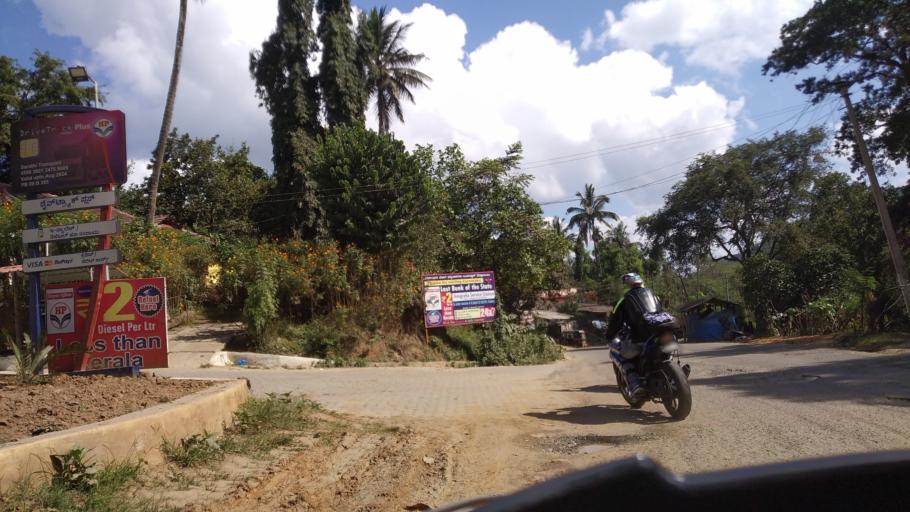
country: IN
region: Karnataka
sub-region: Kodagu
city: Ponnampet
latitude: 11.9673
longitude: 76.0533
